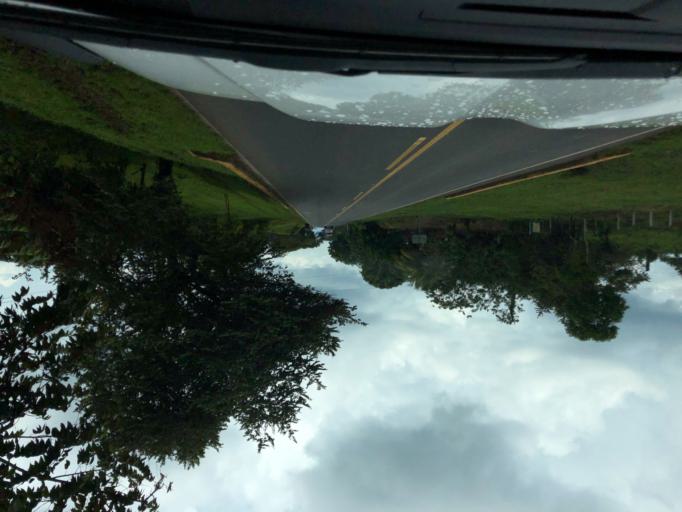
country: NI
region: Chontales
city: Villa Sandino
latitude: 11.9931
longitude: -84.8604
